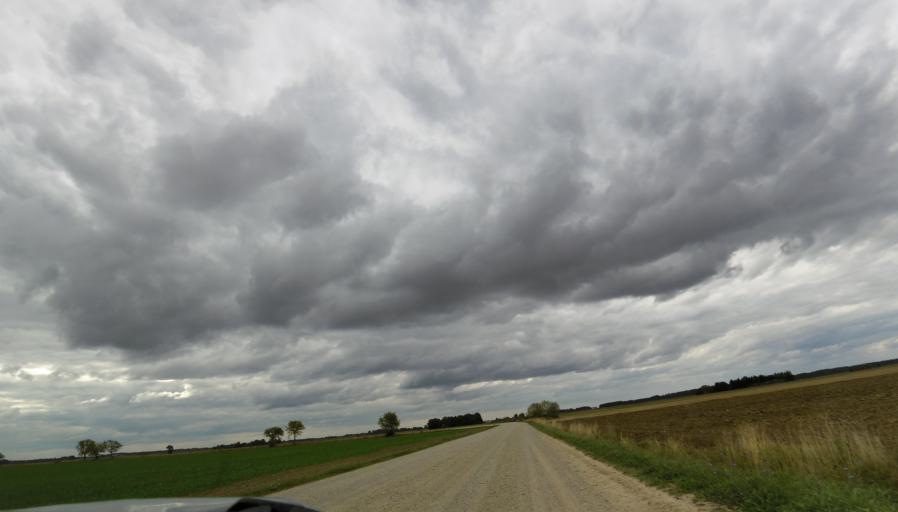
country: LT
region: Panevezys
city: Pasvalys
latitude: 56.0762
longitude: 24.2810
